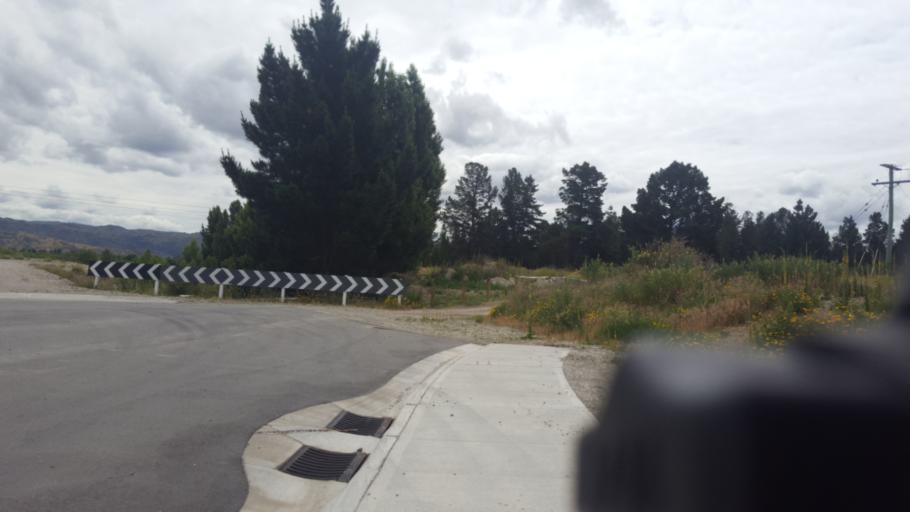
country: NZ
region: Otago
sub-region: Queenstown-Lakes District
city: Wanaka
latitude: -45.2460
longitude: 169.3713
